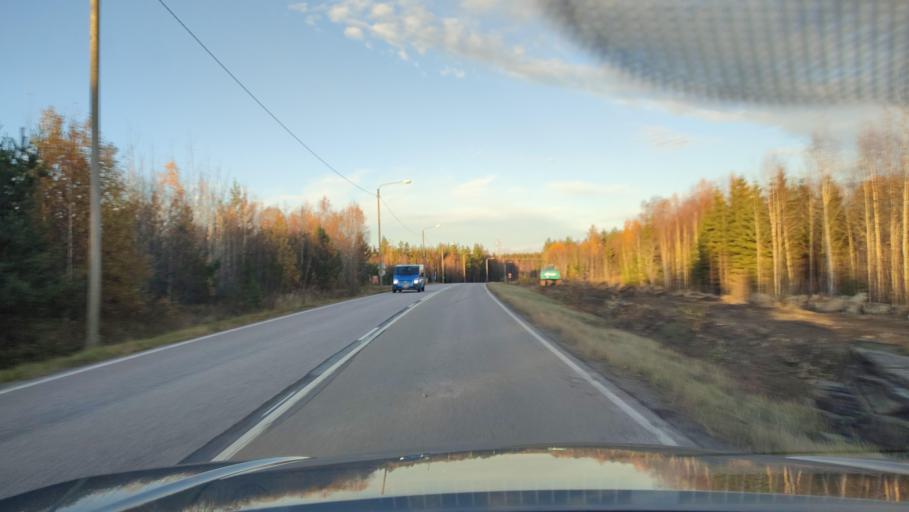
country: FI
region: Ostrobothnia
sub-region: Sydosterbotten
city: Kristinestad
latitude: 62.2941
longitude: 21.3819
